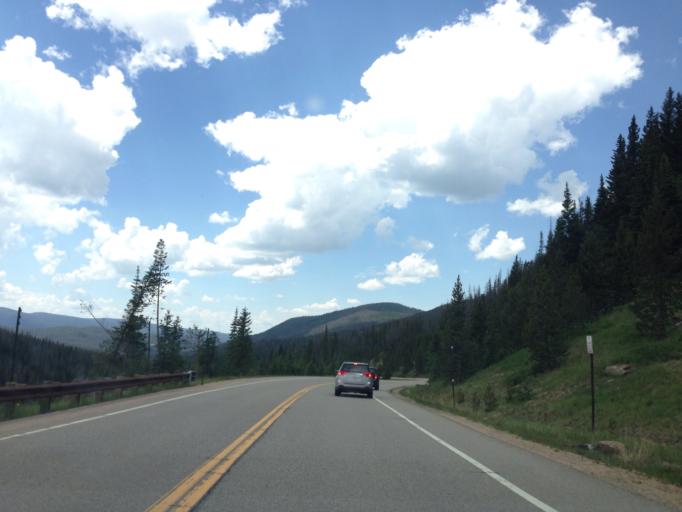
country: US
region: Colorado
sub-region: Larimer County
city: Estes Park
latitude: 40.5044
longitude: -105.9044
